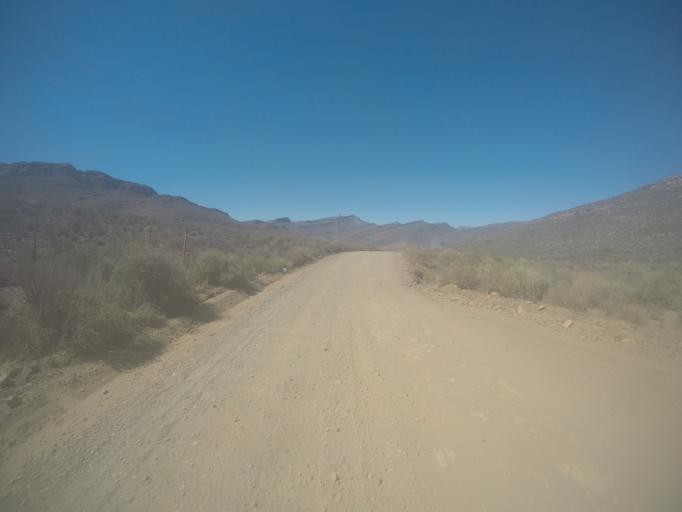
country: ZA
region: Western Cape
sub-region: West Coast District Municipality
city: Clanwilliam
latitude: -32.5439
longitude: 19.3579
